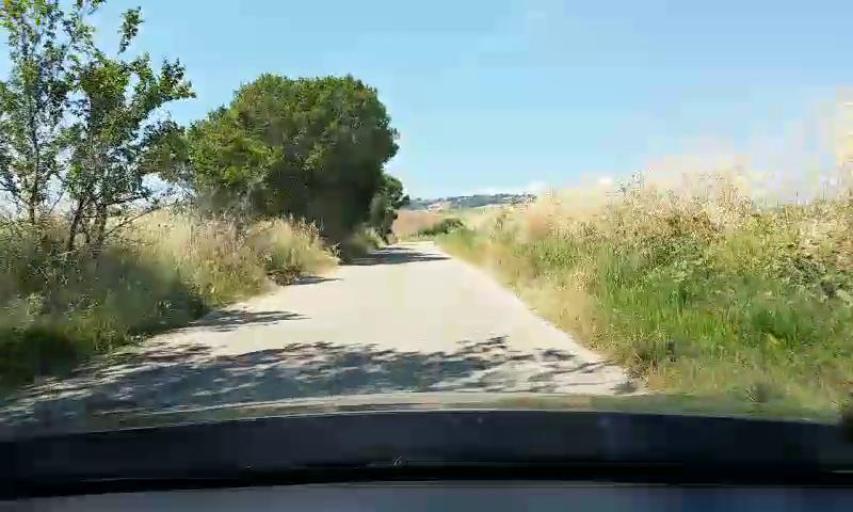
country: IT
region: Molise
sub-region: Provincia di Campobasso
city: Montecilfone
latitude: 41.9281
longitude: 14.8551
